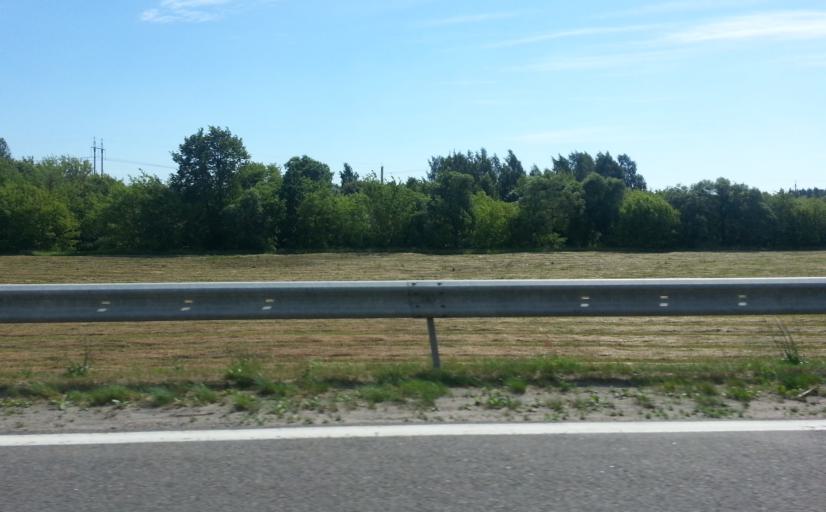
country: LT
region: Panevezys
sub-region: Panevezys City
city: Panevezys
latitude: 55.7377
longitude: 24.2766
